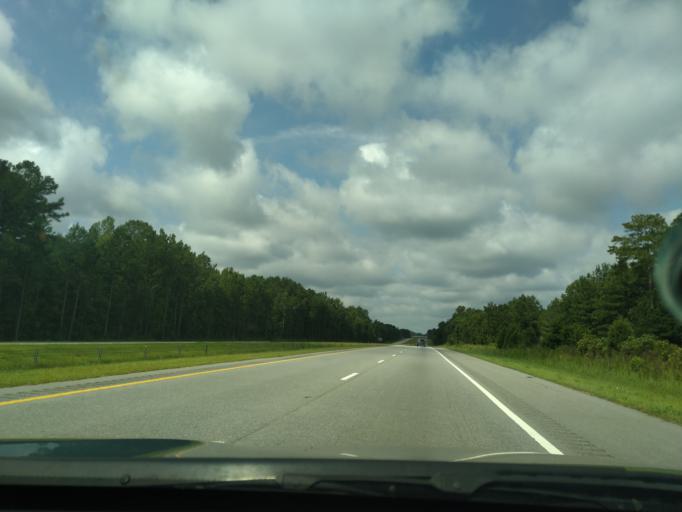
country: US
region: North Carolina
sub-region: Martin County
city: Williamston
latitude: 35.8286
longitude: -77.1306
